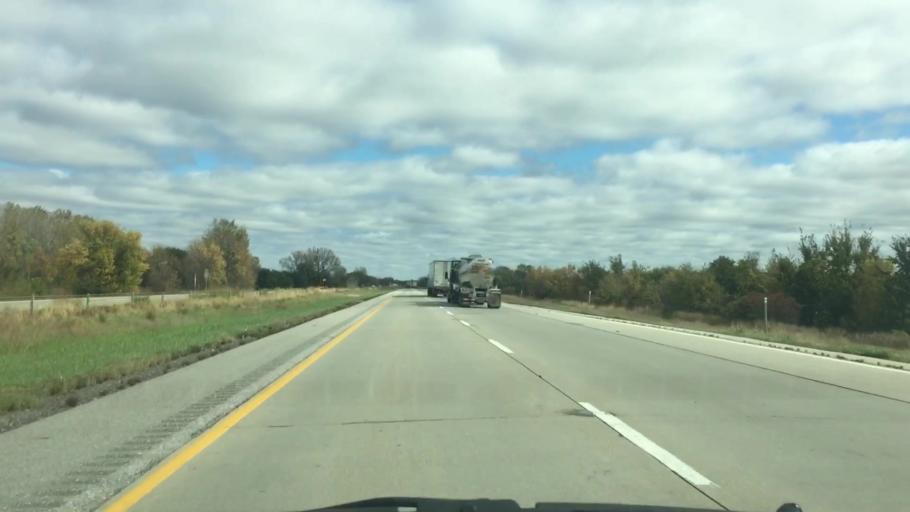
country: US
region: Iowa
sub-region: Jasper County
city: Colfax
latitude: 41.6934
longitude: -93.2404
